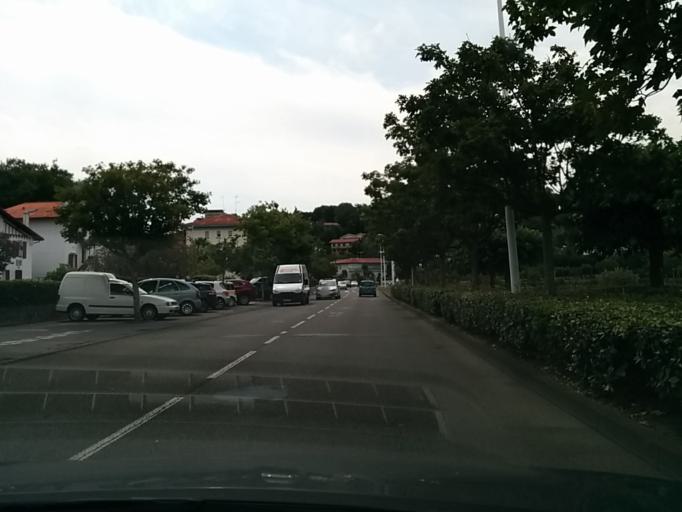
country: FR
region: Aquitaine
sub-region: Departement des Pyrenees-Atlantiques
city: Hendaye
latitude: 43.3669
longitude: -1.7708
